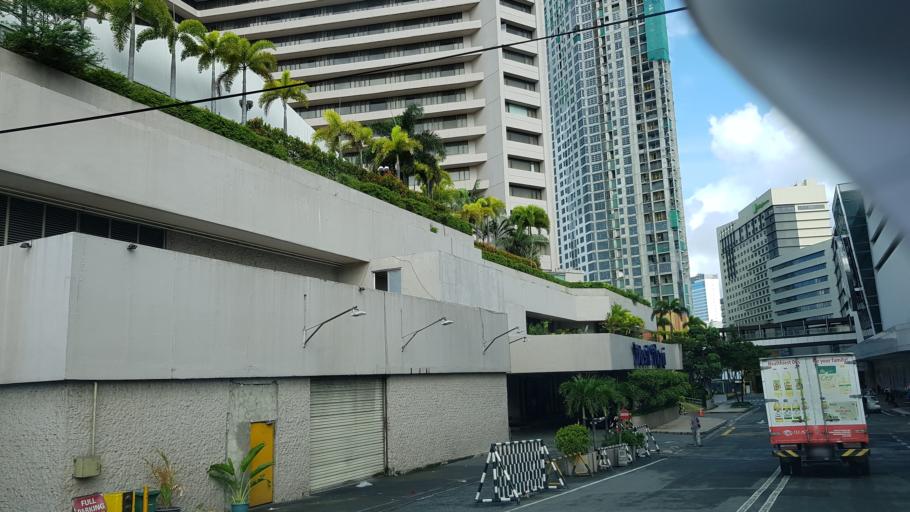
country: PH
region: Metro Manila
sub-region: Makati City
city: Makati City
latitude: 14.5485
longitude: 121.0270
